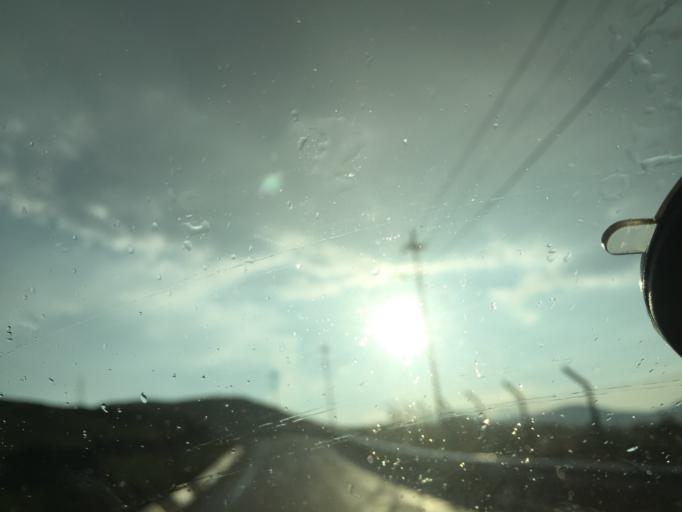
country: LS
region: Maseru
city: Nako
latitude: -29.4786
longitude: 28.0591
